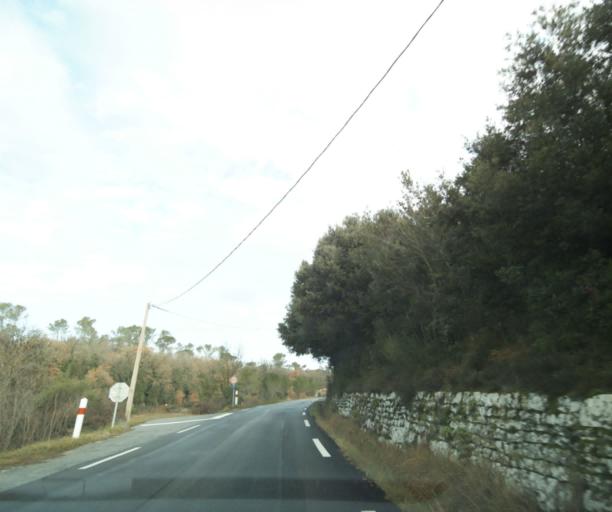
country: FR
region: Provence-Alpes-Cote d'Azur
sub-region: Departement du Var
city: Tourves
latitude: 43.4164
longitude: 5.9260
